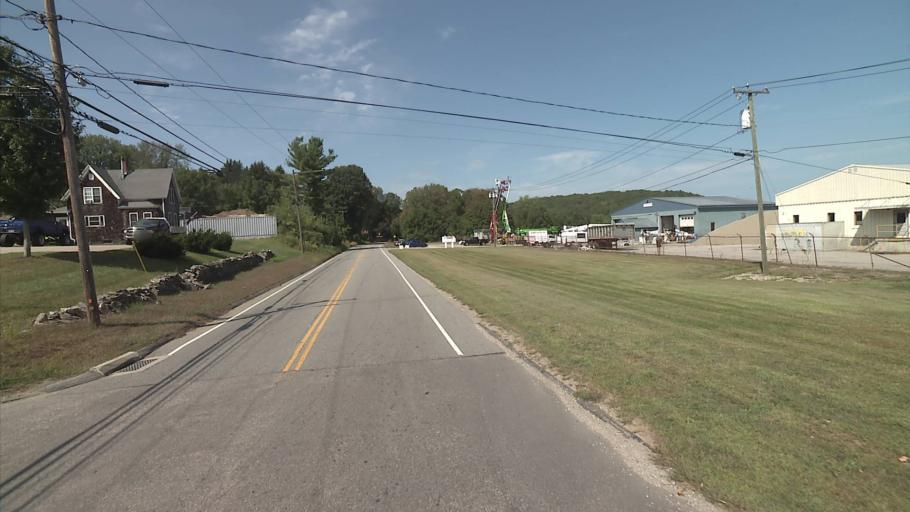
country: US
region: Connecticut
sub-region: New London County
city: Baltic
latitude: 41.5750
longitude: -72.1375
